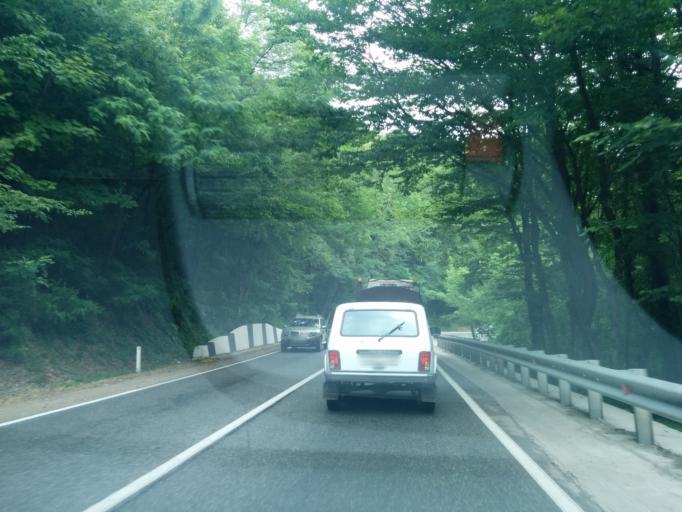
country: RU
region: Krasnodarskiy
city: Agoy
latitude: 44.1296
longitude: 39.0463
